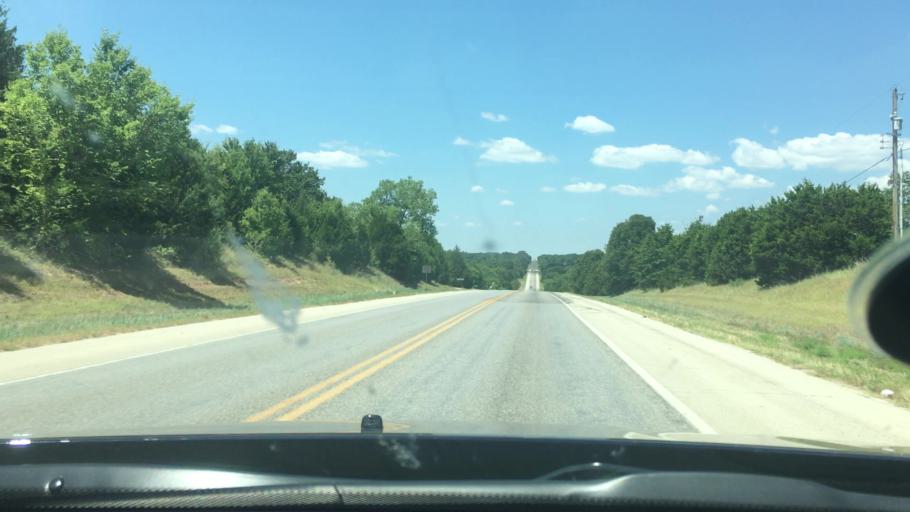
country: US
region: Oklahoma
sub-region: Carter County
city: Dickson
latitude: 34.1873
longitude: -96.9285
